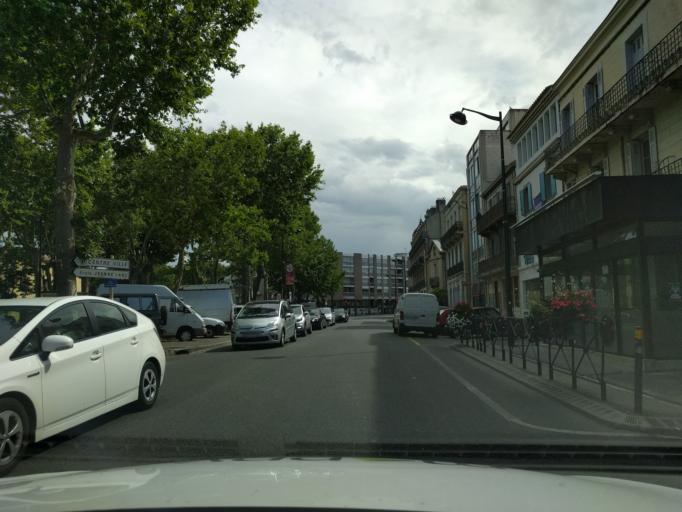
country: FR
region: Languedoc-Roussillon
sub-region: Departement de l'Aude
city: Carcassonne
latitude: 43.2137
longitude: 2.3467
